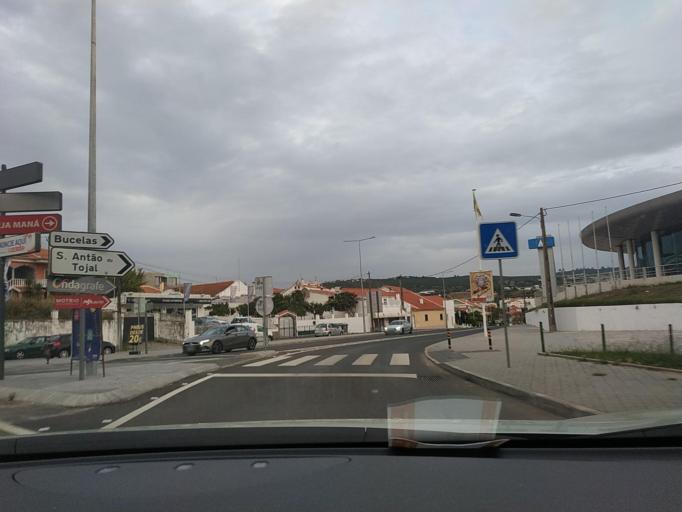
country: PT
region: Lisbon
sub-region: Loures
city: Loures
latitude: 38.8436
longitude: -9.1621
